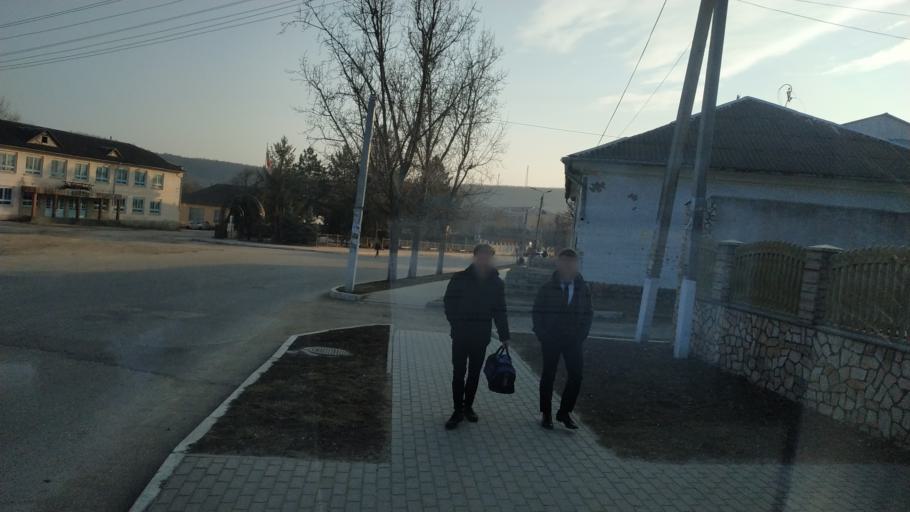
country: MD
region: Hincesti
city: Dancu
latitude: 46.7625
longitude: 28.3587
